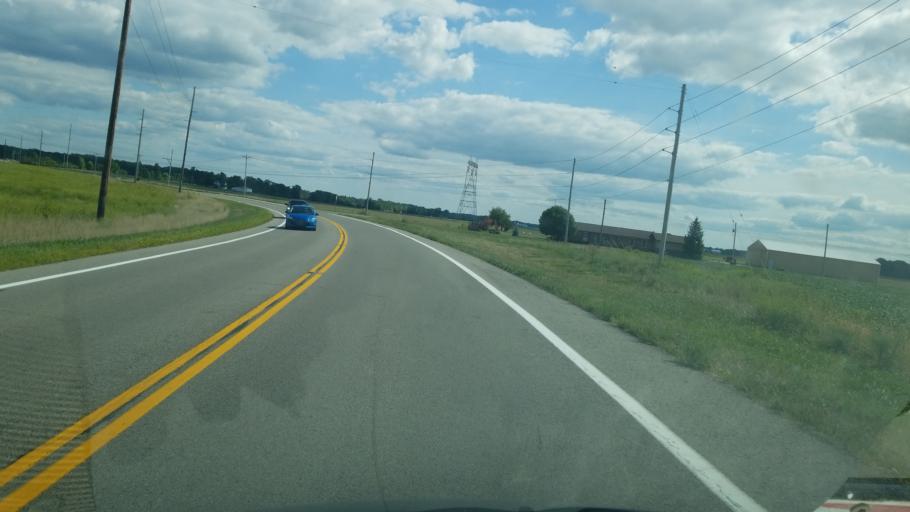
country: US
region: Ohio
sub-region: Logan County
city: Lakeview
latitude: 40.4595
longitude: -83.9176
